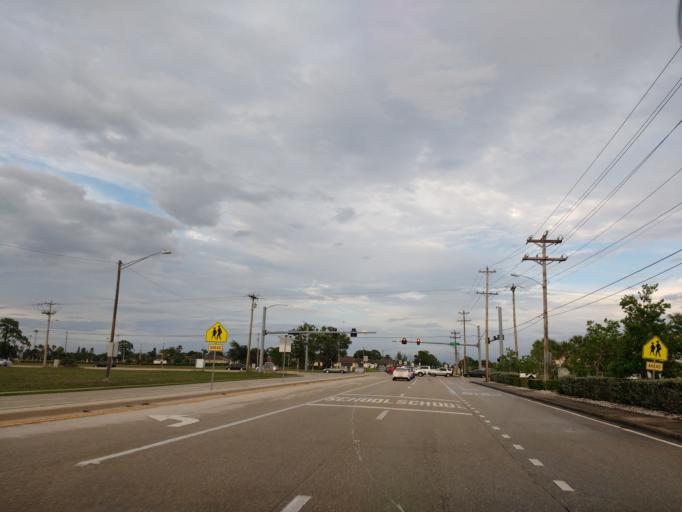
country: US
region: Florida
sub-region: Lee County
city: Cape Coral
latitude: 26.6229
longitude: -81.9923
